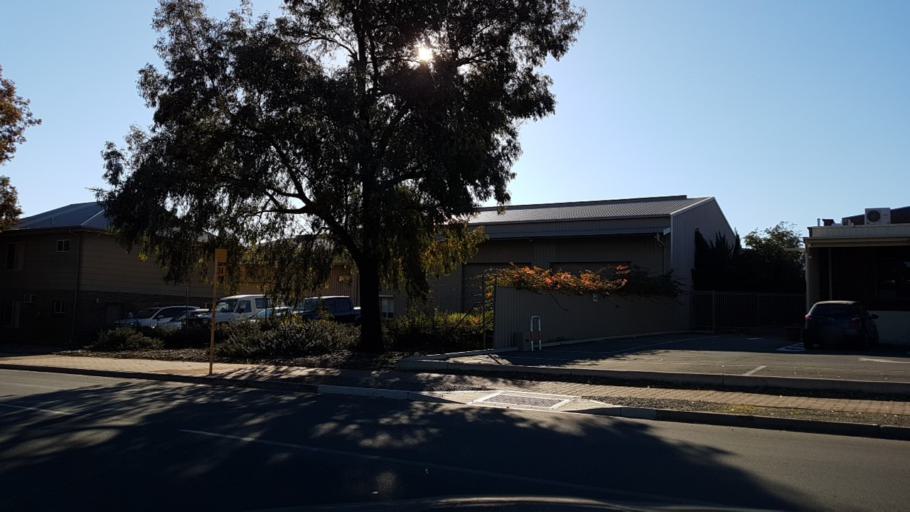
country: AU
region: South Australia
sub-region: Campbelltown
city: Paradise
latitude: -34.8811
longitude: 138.6841
